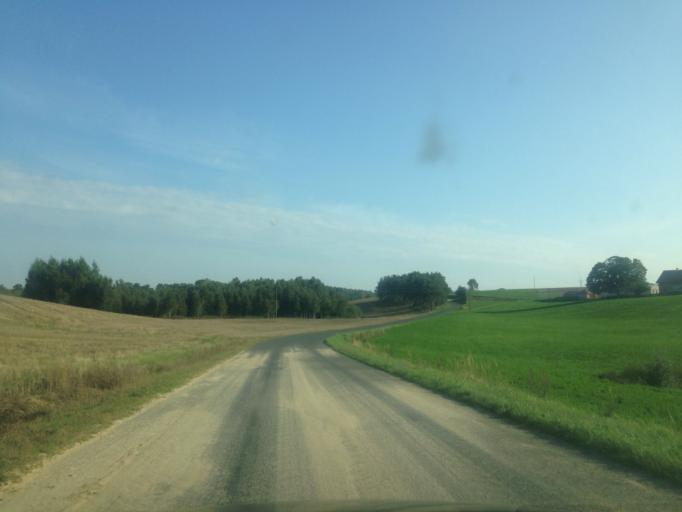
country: PL
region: Kujawsko-Pomorskie
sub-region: Powiat brodnicki
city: Brzozie
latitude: 53.2967
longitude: 19.6886
